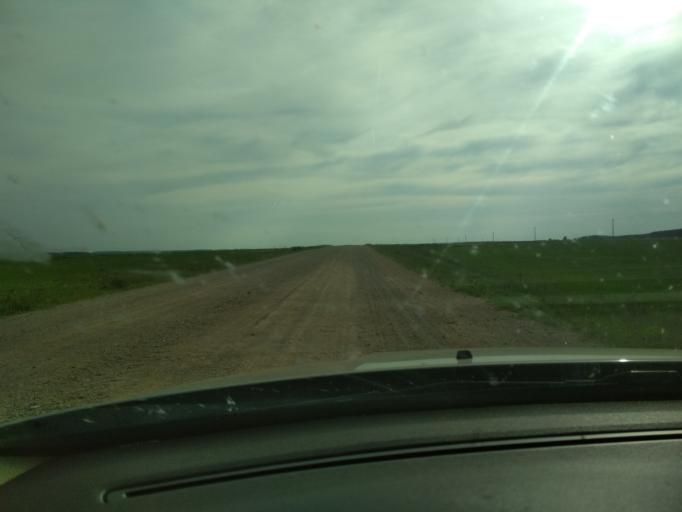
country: BY
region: Grodnenskaya
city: Mir
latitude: 53.3913
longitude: 26.3995
